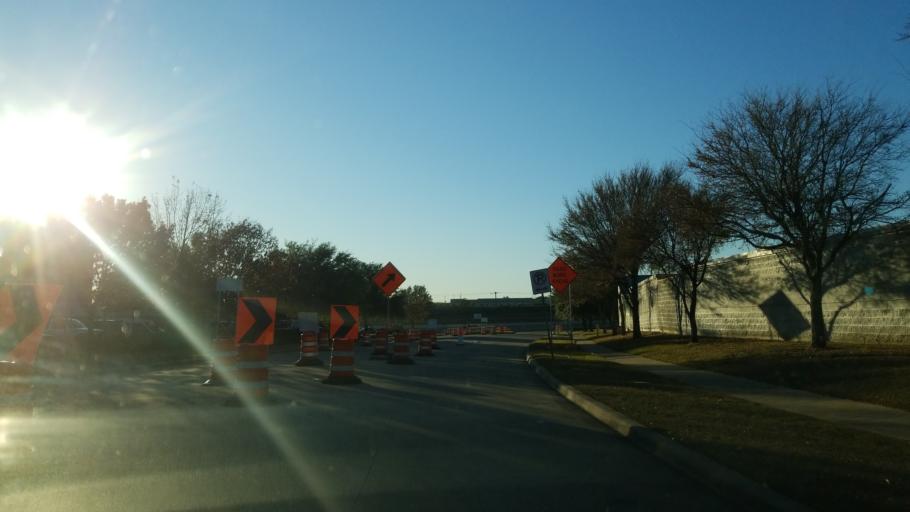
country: US
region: Texas
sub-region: Tarrant County
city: Arlington
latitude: 32.7339
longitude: -97.0603
